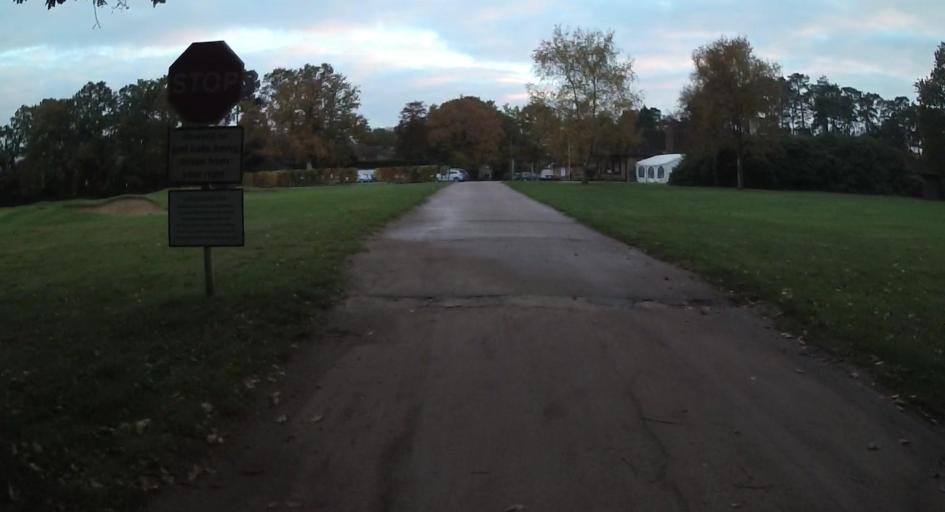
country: GB
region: England
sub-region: Bracknell Forest
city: Crowthorne
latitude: 51.3719
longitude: -0.8178
